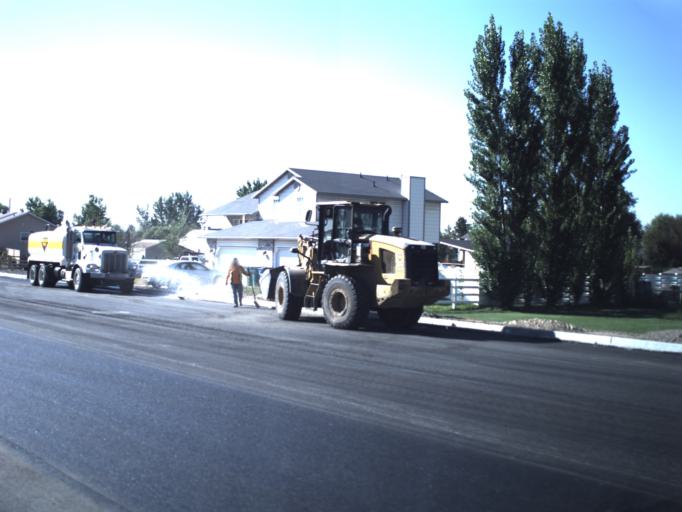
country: US
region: Utah
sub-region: Weber County
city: West Haven
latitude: 41.1907
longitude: -112.0839
